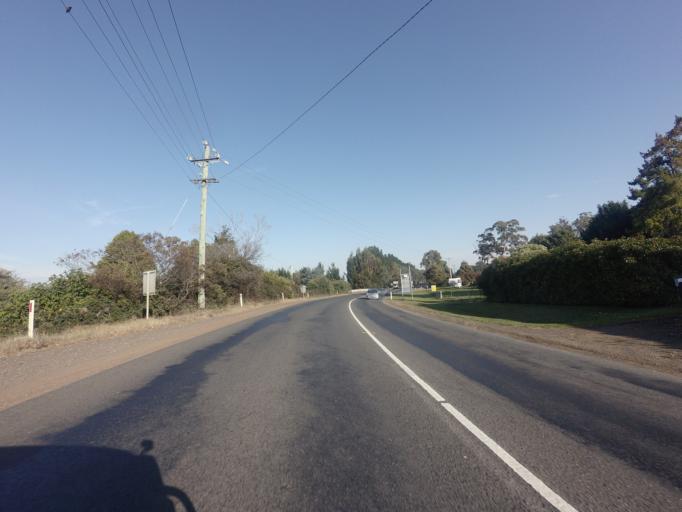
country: AU
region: Tasmania
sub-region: Northern Midlands
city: Perth
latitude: -41.5782
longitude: 147.1591
